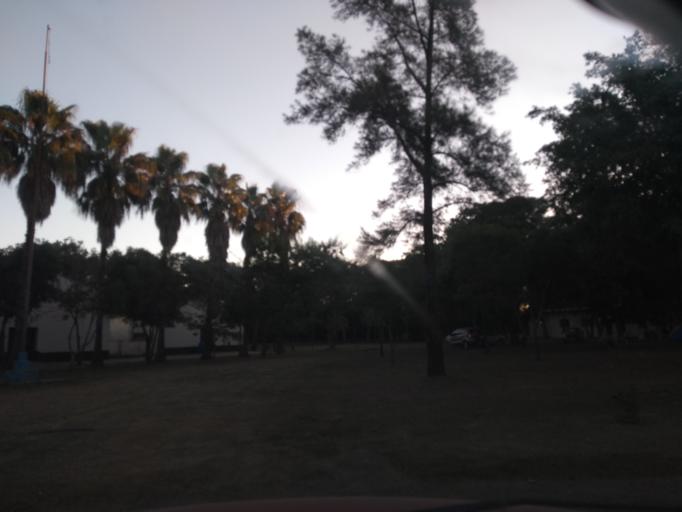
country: AR
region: Chaco
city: Fontana
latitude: -27.4250
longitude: -59.0047
